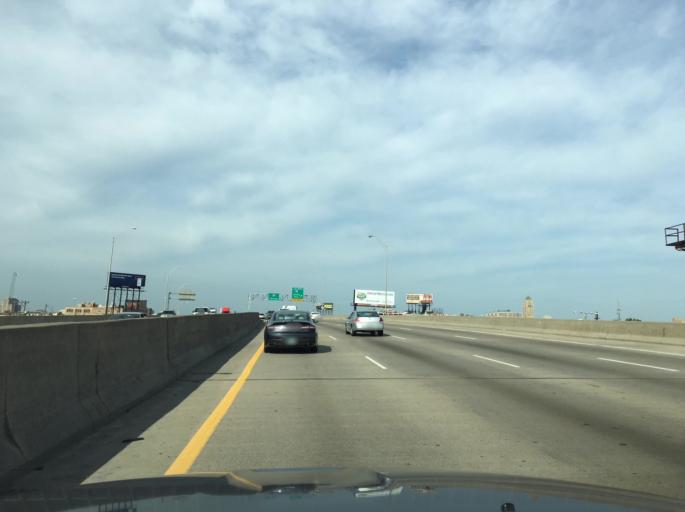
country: US
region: Michigan
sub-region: Wayne County
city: Hamtramck
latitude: 42.3724
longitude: -83.0518
